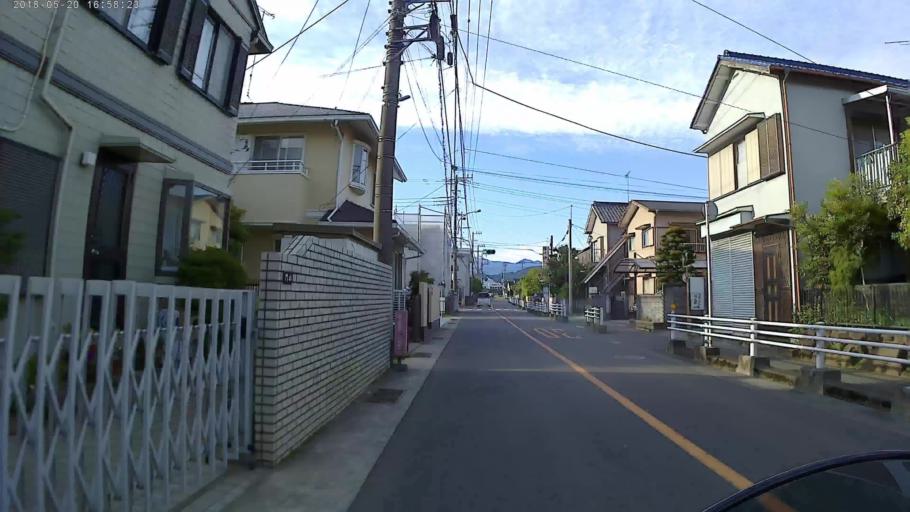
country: JP
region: Kanagawa
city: Odawara
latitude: 35.2824
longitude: 139.1776
